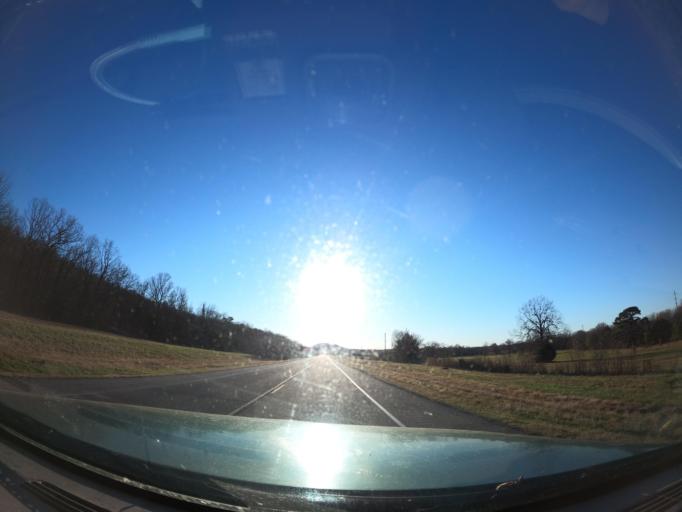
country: US
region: Oklahoma
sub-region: Pittsburg County
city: Hartshorne
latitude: 34.8724
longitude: -95.5136
